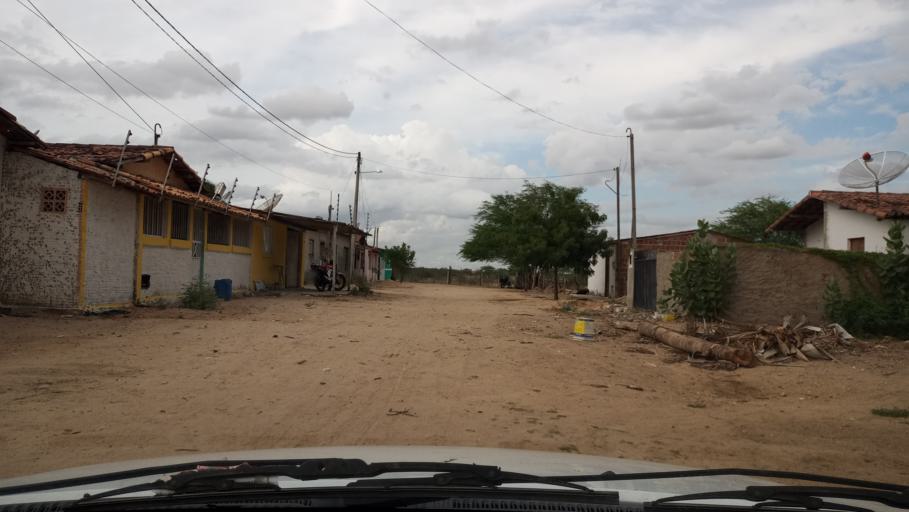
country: BR
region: Rio Grande do Norte
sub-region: Tangara
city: Tangara
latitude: -6.1916
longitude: -35.7995
